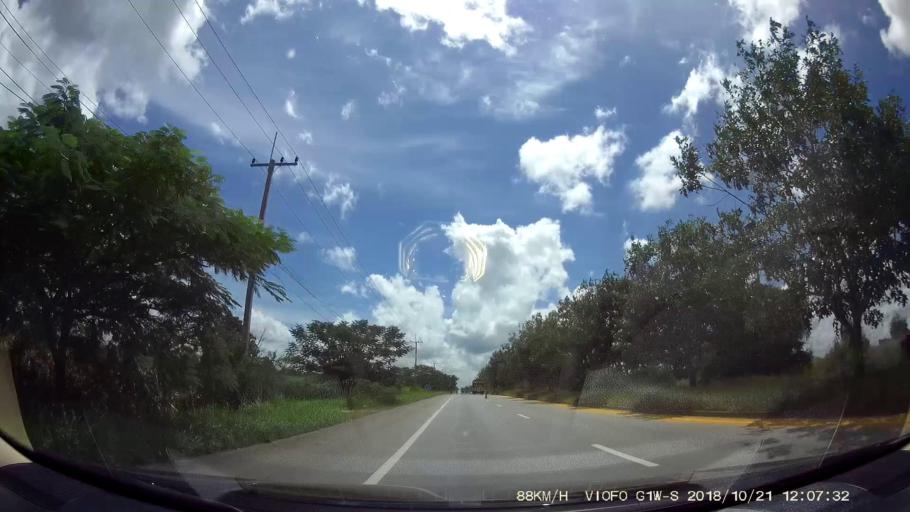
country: TH
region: Chaiyaphum
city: Chatturat
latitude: 15.4469
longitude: 101.8284
